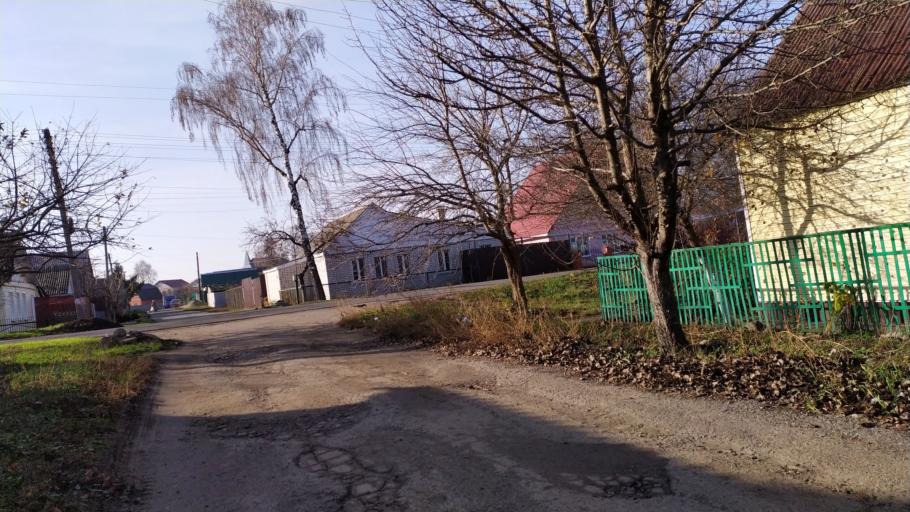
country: RU
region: Kursk
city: Kursk
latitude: 51.6452
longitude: 36.1420
